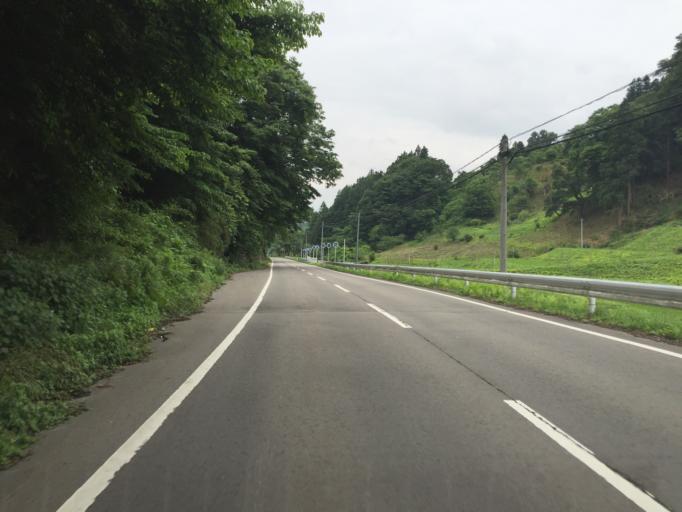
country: JP
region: Fukushima
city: Nihommatsu
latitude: 37.6256
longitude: 140.5593
